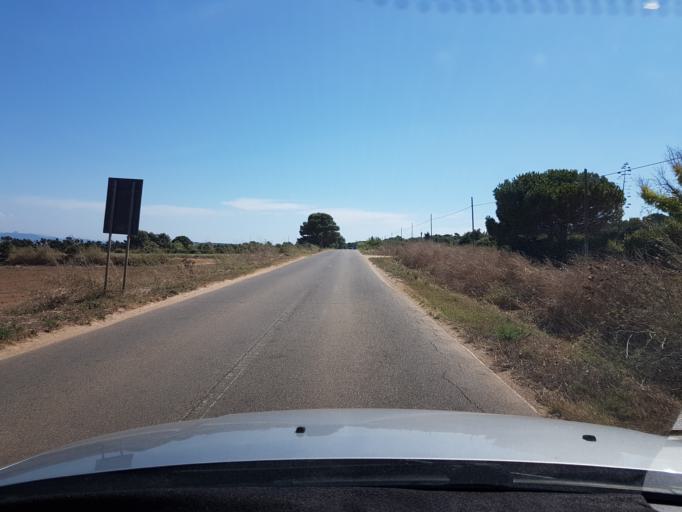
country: IT
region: Sardinia
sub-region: Provincia di Oristano
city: Cabras
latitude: 39.9069
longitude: 8.4379
